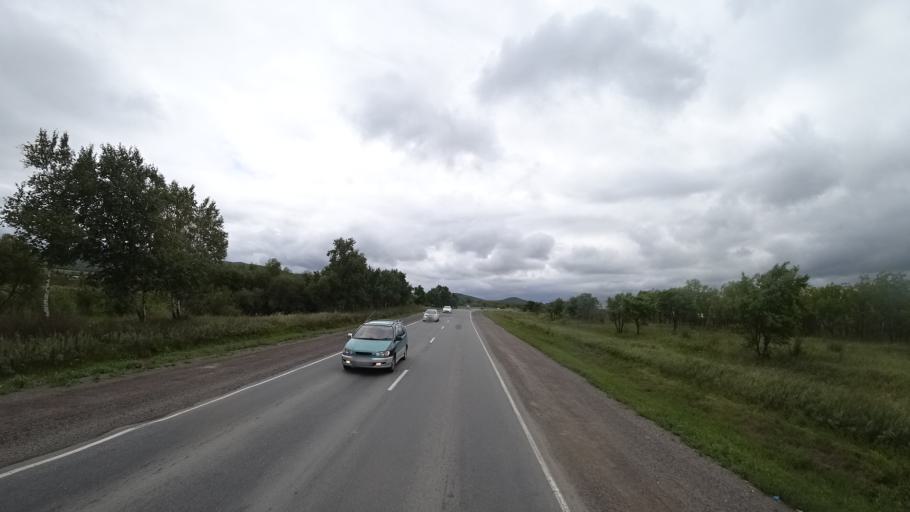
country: RU
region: Primorskiy
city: Chernigovka
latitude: 44.3239
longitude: 132.5702
